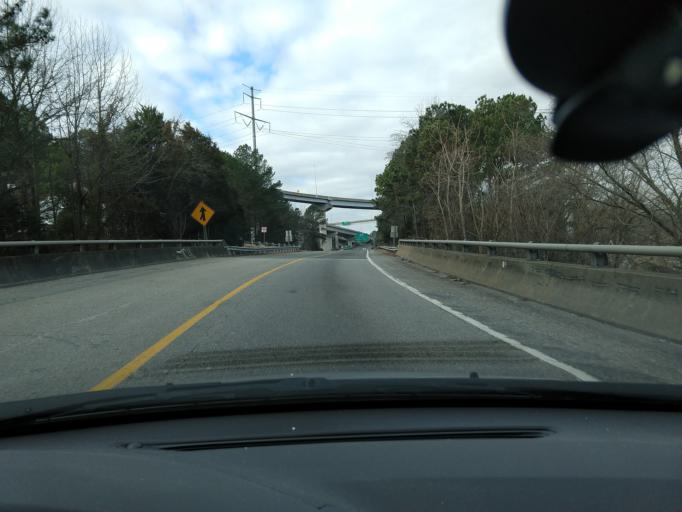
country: US
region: Virginia
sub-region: Chesterfield County
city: Bensley
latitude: 37.4440
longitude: -77.4261
